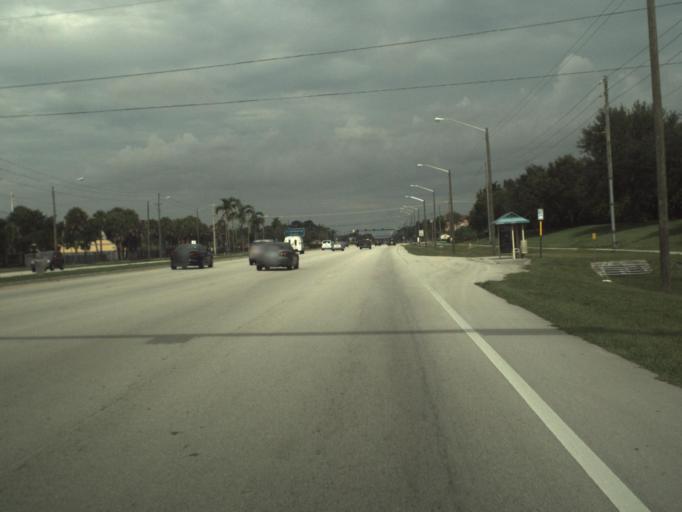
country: US
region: Florida
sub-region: Palm Beach County
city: Plantation Mobile Home Park
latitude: 26.7086
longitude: -80.1660
